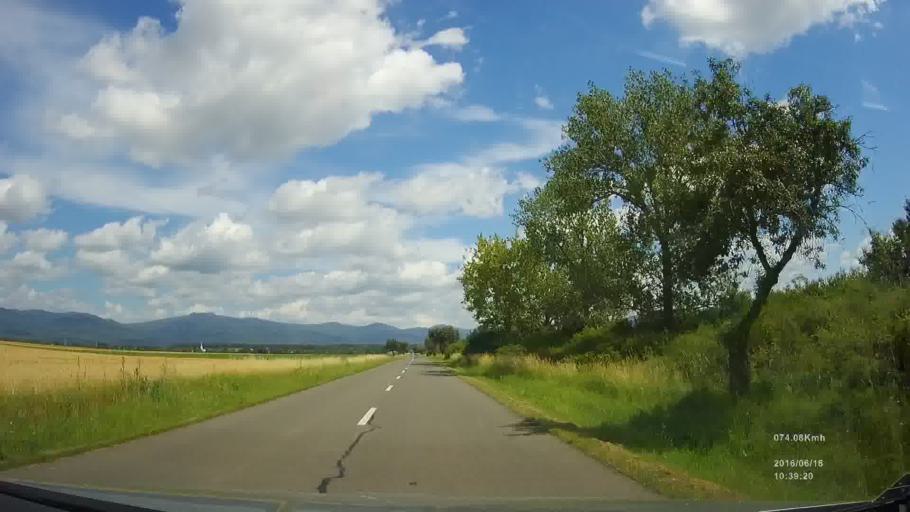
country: SK
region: Kosicky
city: Sobrance
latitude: 48.7719
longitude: 22.1261
